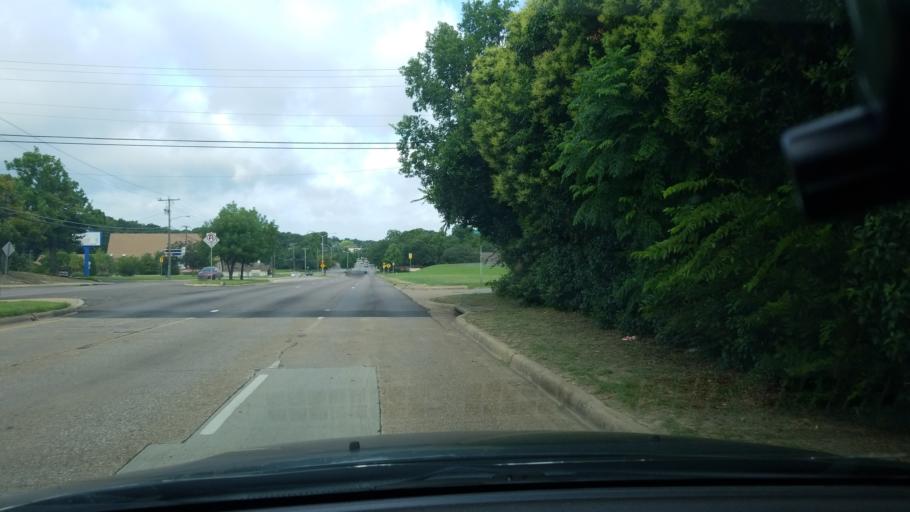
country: US
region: Texas
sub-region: Dallas County
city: Highland Park
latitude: 32.8158
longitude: -96.6929
